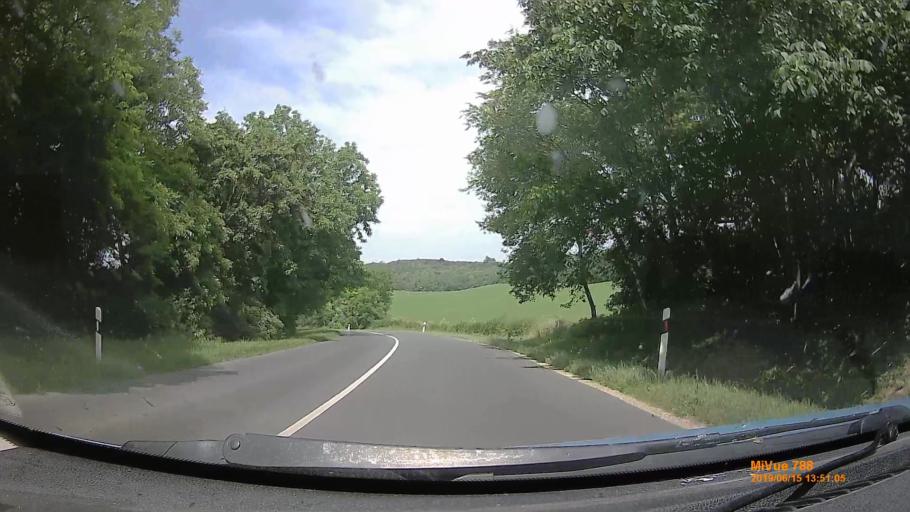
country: HU
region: Tolna
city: Iregszemcse
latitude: 46.7494
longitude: 18.1658
